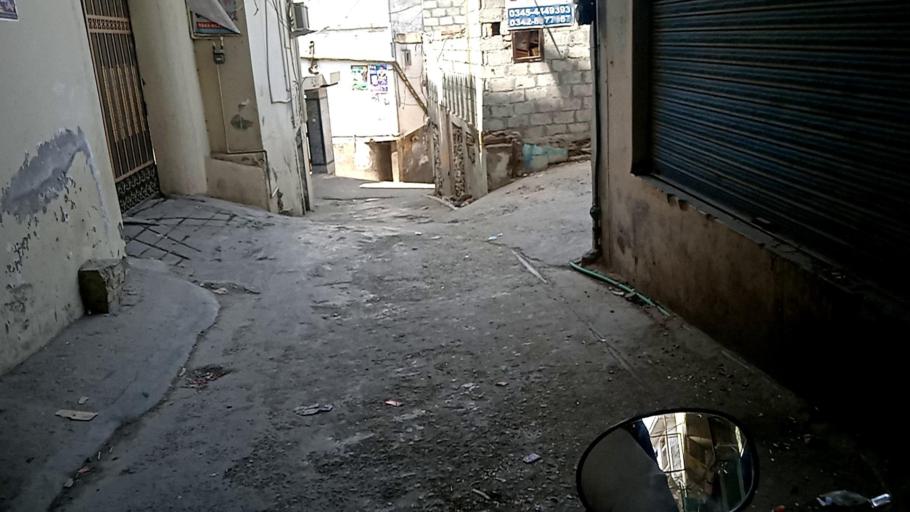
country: PK
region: Khyber Pakhtunkhwa
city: Mingora
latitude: 34.7758
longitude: 72.3571
